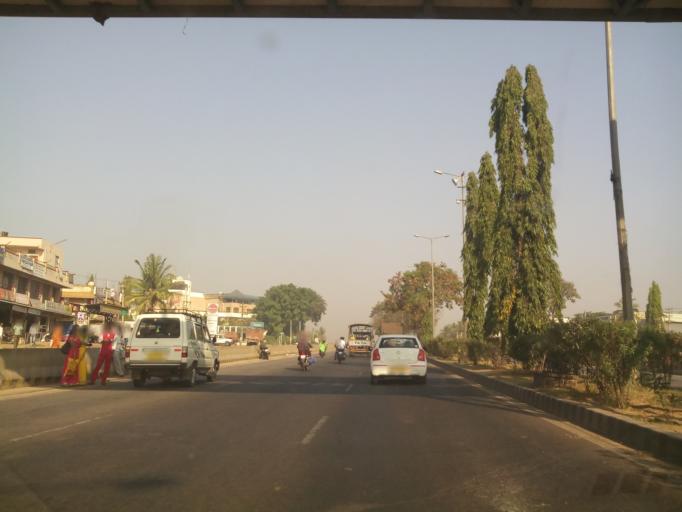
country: IN
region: Karnataka
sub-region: Bangalore Rural
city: Nelamangala
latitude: 13.0655
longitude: 77.4538
